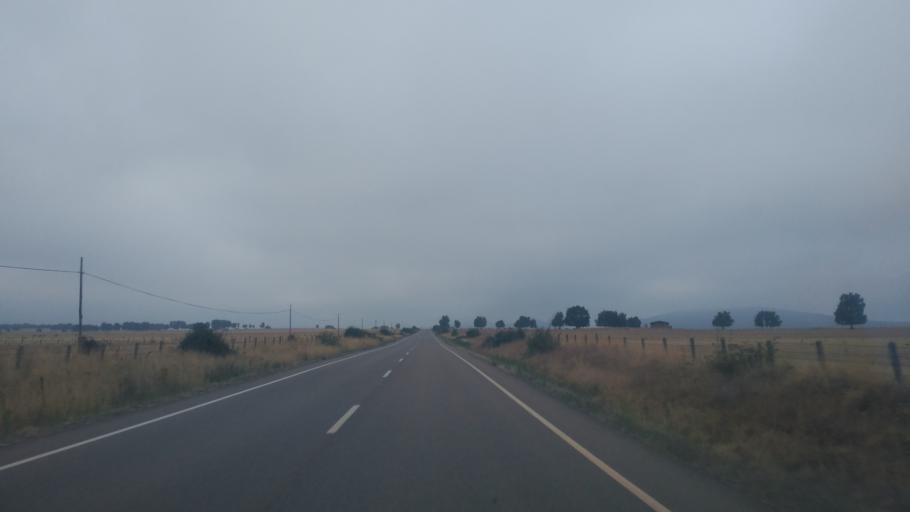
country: ES
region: Castille and Leon
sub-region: Provincia de Salamanca
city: Tamames
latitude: 40.6433
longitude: -6.1132
